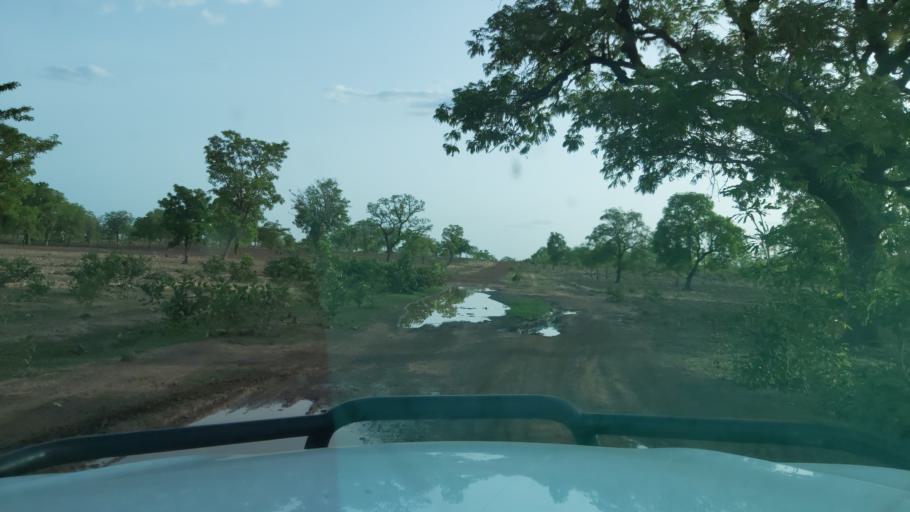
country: ML
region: Koulikoro
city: Kolokani
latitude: 13.2124
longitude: -7.9014
